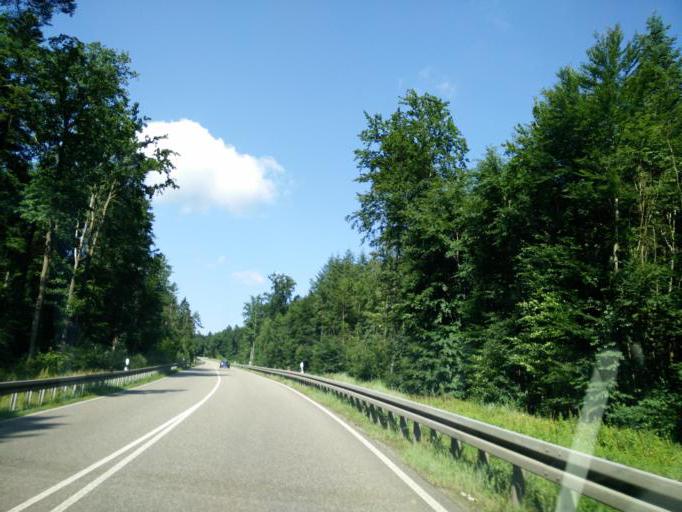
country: DE
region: Baden-Wuerttemberg
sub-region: Karlsruhe Region
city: Niefern-Oschelbronn
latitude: 48.8797
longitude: 8.7806
